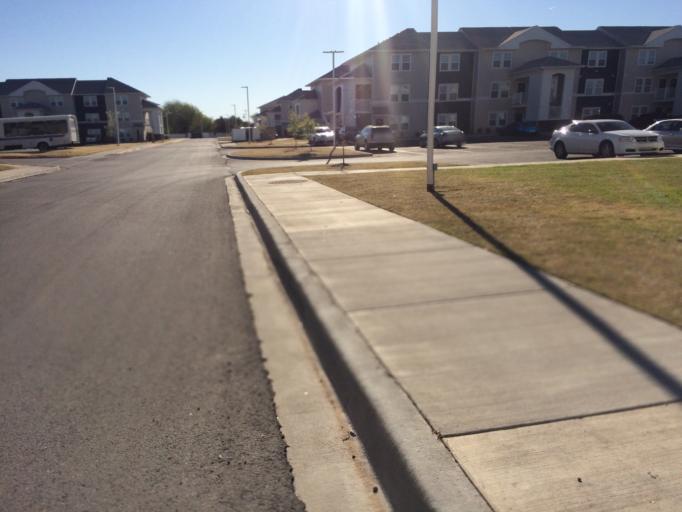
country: US
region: Oklahoma
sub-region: Cleveland County
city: Noble
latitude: 35.1776
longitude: -97.4188
